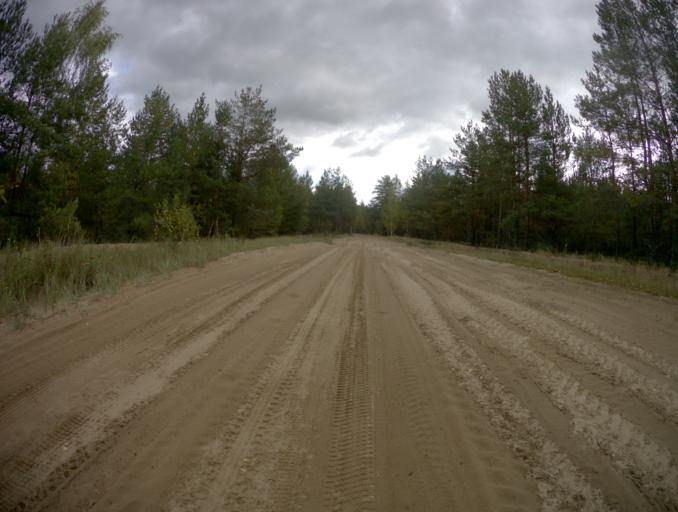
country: RU
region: Vladimir
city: Petushki
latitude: 55.8857
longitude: 39.5072
